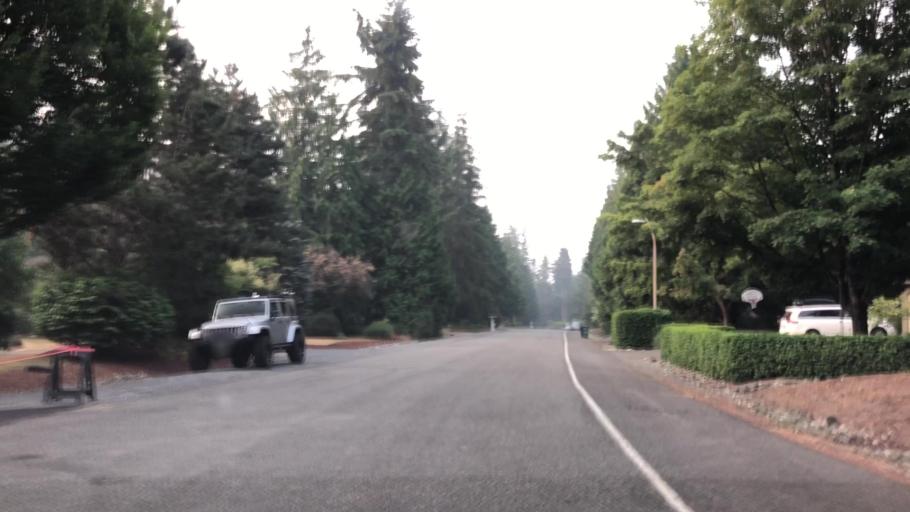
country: US
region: Washington
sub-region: King County
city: Cottage Lake
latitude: 47.7279
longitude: -122.1010
